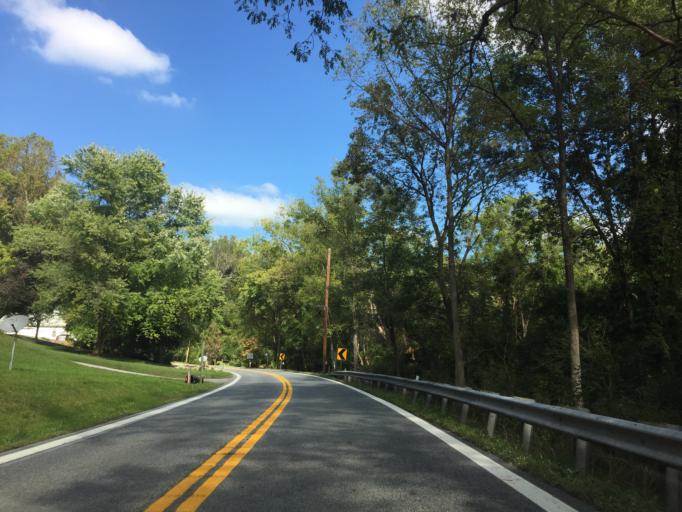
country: US
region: Maryland
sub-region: Baltimore County
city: Perry Hall
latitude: 39.4219
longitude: -76.4966
